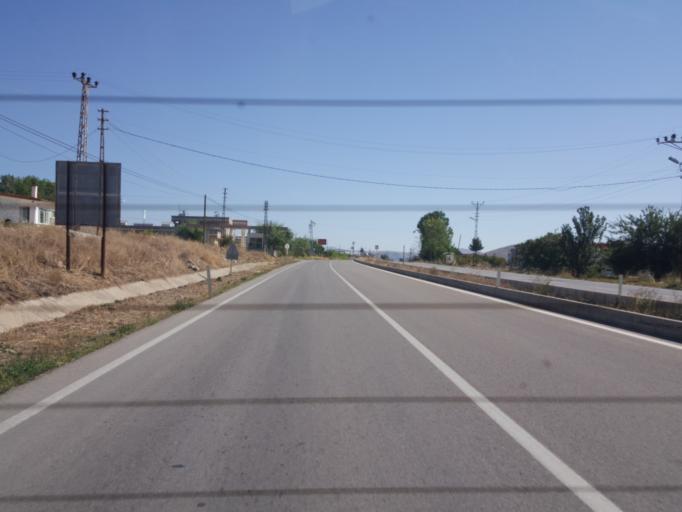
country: TR
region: Tokat
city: Zile
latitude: 40.3099
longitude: 35.9073
